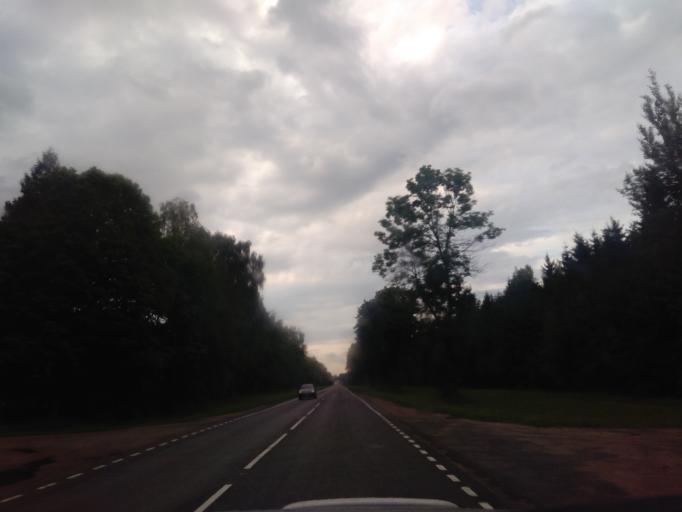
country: BY
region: Minsk
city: Enyerhyetykaw
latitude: 53.5731
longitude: 27.0614
